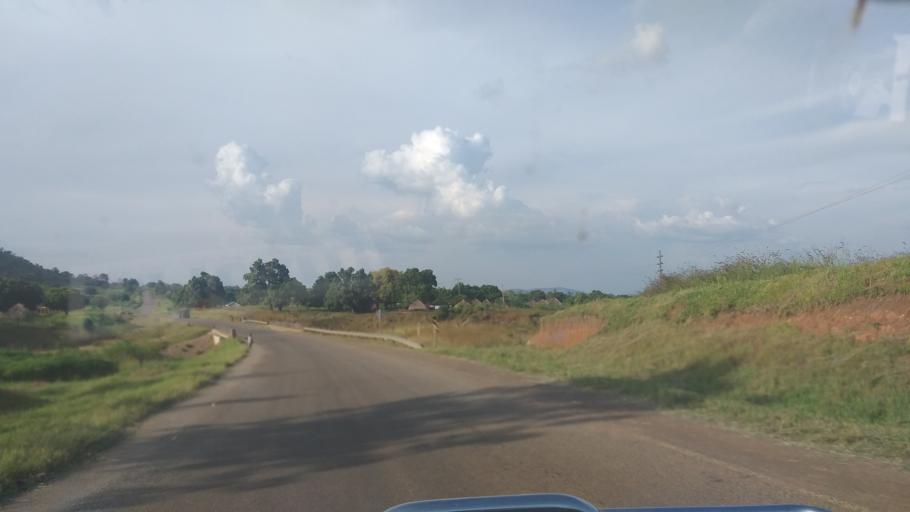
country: UG
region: Northern Region
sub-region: Arua District
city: Arua
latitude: 2.8286
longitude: 30.9954
